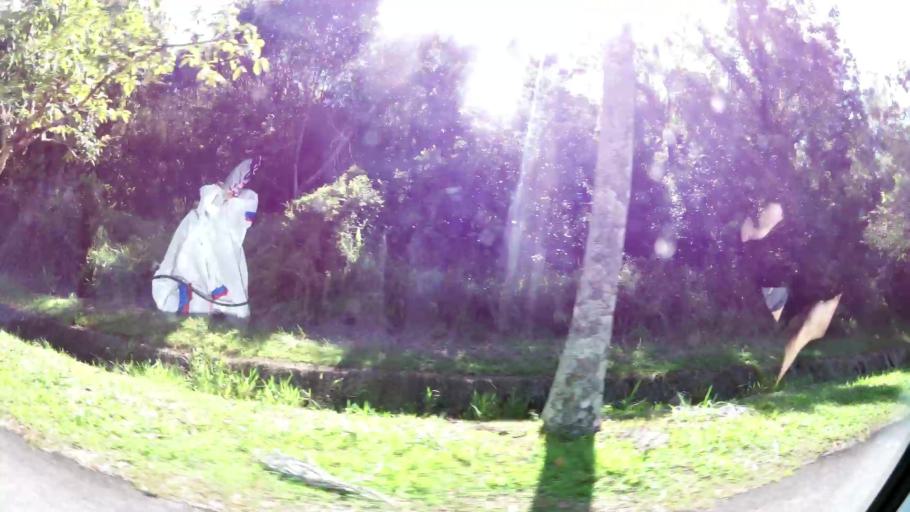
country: BN
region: Brunei and Muara
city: Bandar Seri Begawan
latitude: 4.9484
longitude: 114.9369
